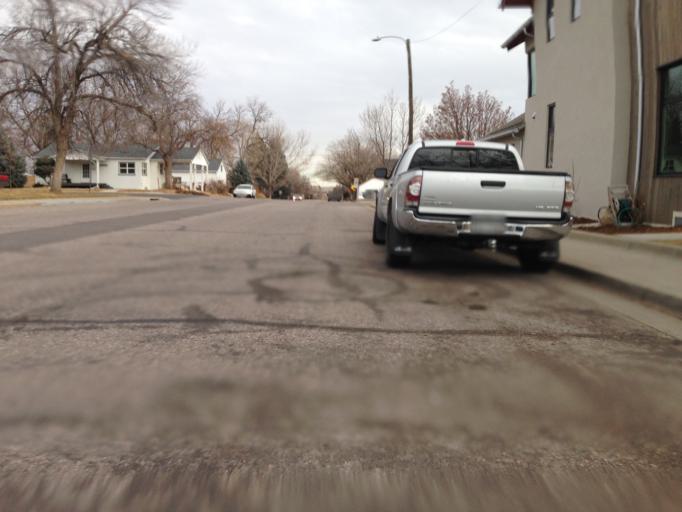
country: US
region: Colorado
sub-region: Boulder County
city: Louisville
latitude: 39.9826
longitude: -105.1364
